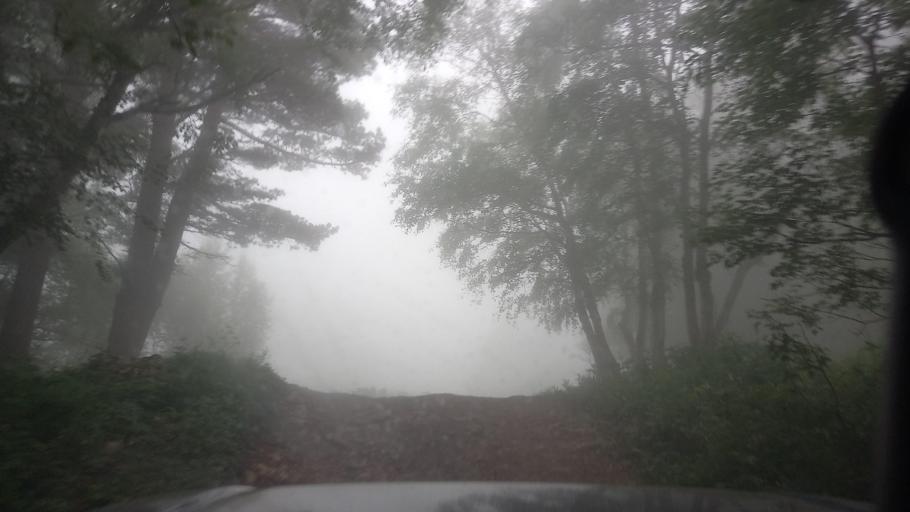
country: RU
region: Karachayevo-Cherkesiya
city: Kurdzhinovo
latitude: 43.7973
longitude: 40.8460
